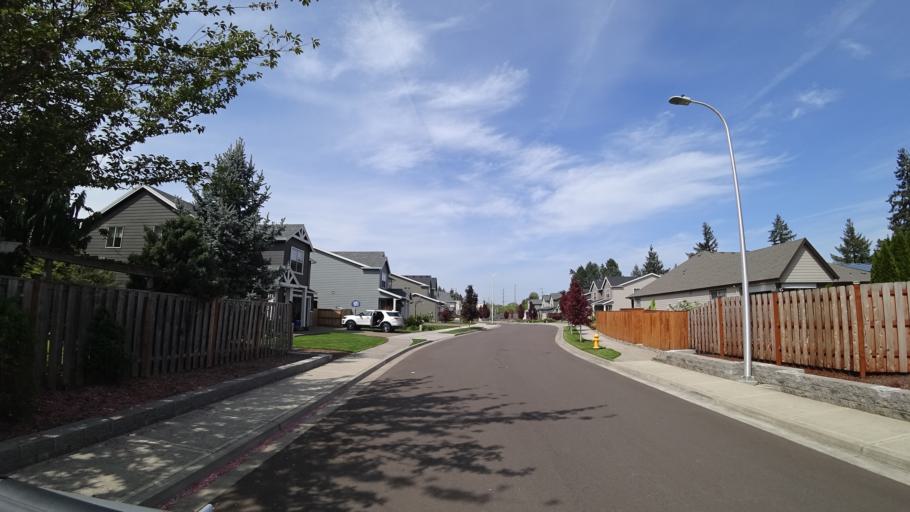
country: US
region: Oregon
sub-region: Washington County
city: Hillsboro
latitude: 45.5273
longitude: -122.9330
